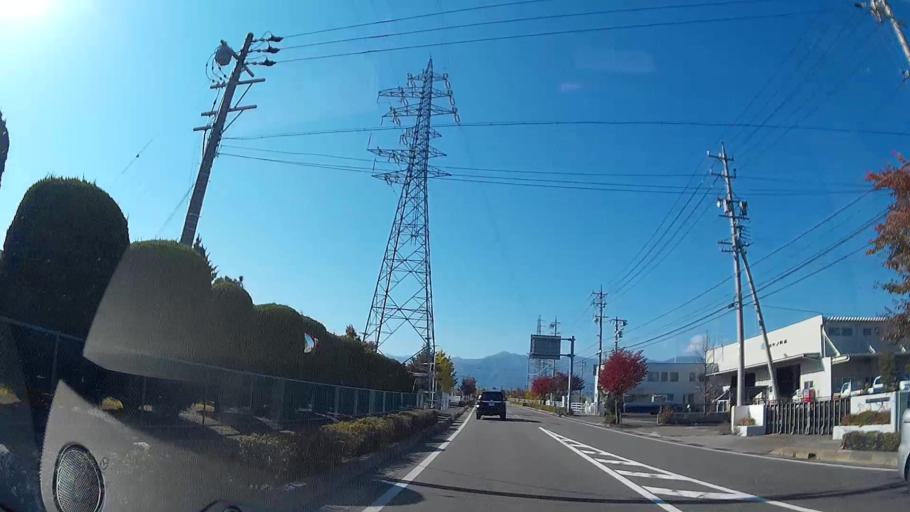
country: JP
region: Nagano
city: Matsumoto
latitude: 36.2051
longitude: 137.9339
